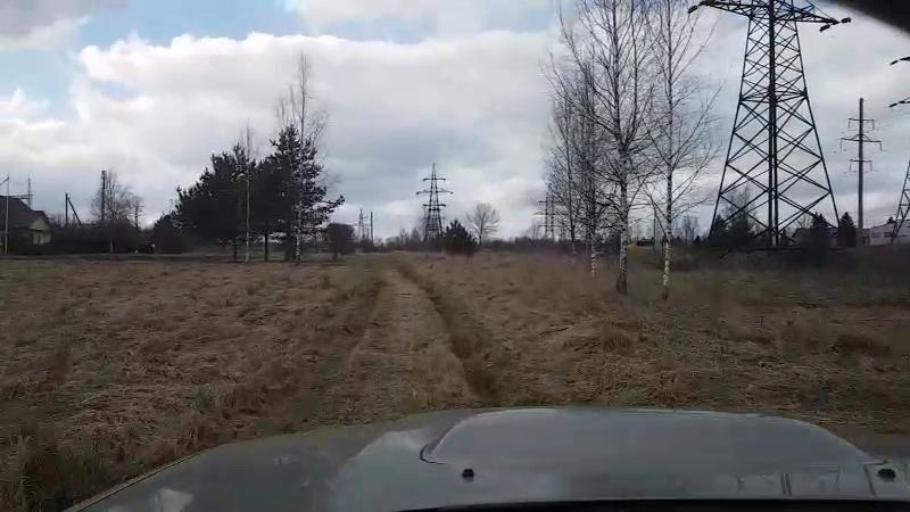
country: EE
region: Jaervamaa
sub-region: Paide linn
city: Paide
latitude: 58.8762
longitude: 25.5364
